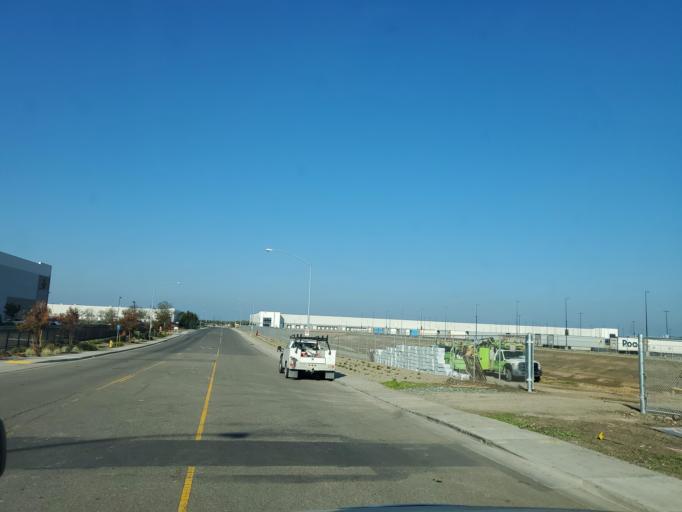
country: US
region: California
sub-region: San Joaquin County
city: Kennedy
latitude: 37.9089
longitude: -121.1932
